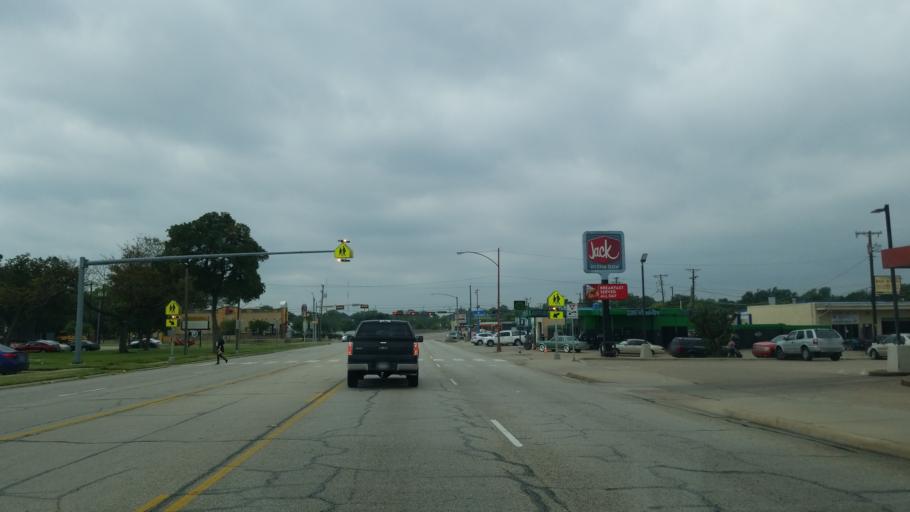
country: US
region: Texas
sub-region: Dallas County
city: Garland
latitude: 32.9102
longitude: -96.6481
